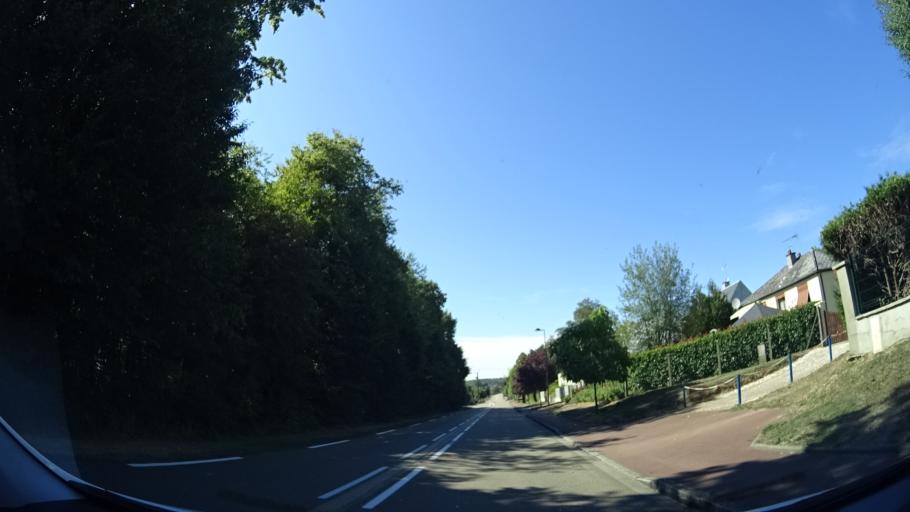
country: FR
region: Centre
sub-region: Departement du Loiret
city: Douchy
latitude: 47.9399
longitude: 3.0634
